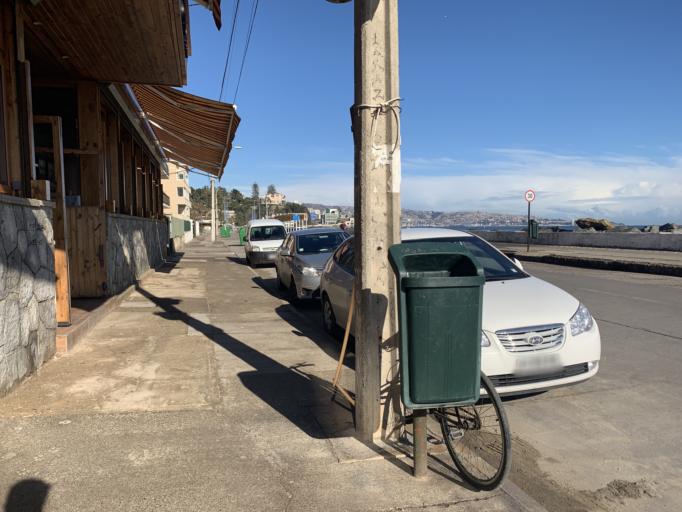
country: CL
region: Valparaiso
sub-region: Provincia de Valparaiso
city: Vina del Mar
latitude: -33.0163
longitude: -71.5585
